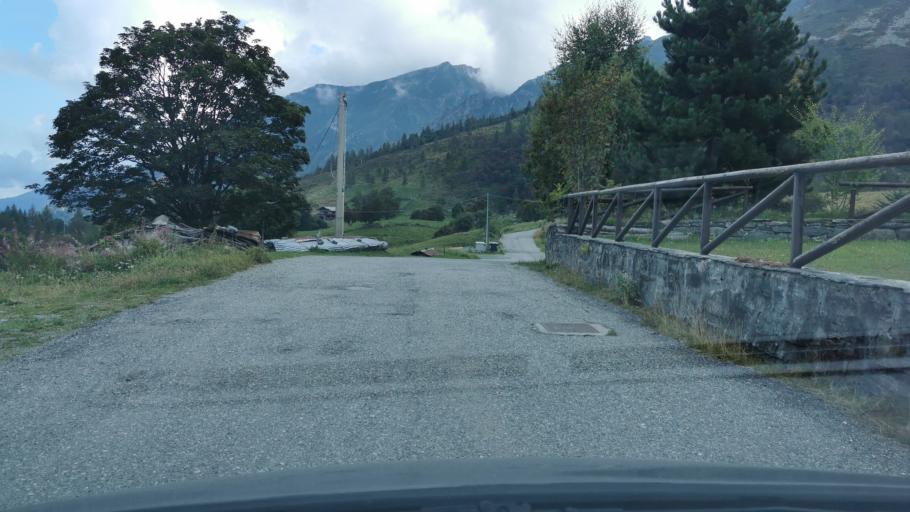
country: IT
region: Piedmont
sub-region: Provincia di Torino
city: Usseglio
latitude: 45.2217
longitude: 7.2314
